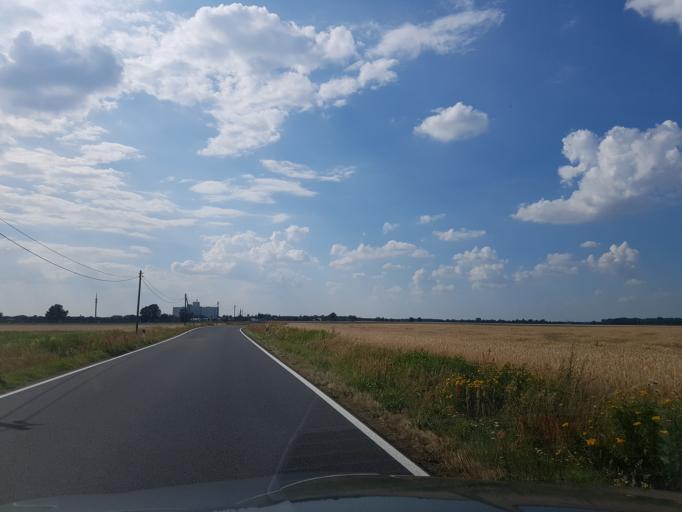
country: DE
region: Brandenburg
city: Herzberg
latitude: 51.6887
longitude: 13.2808
